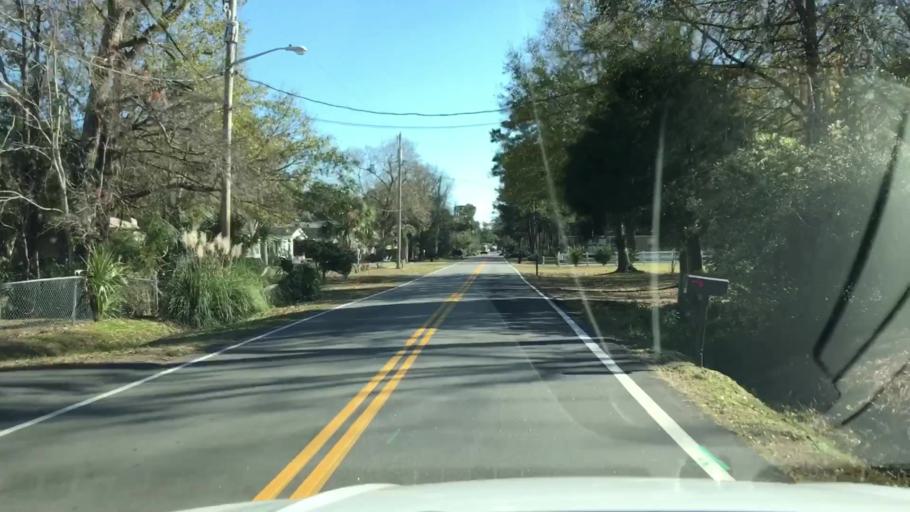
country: US
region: South Carolina
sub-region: Horry County
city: Garden City
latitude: 33.5934
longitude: -79.0004
